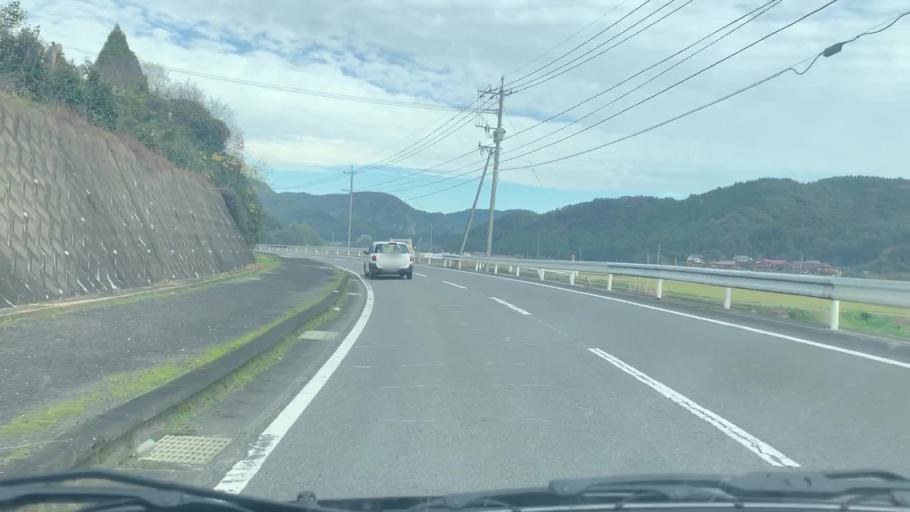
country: JP
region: Saga Prefecture
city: Imaricho-ko
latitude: 33.3124
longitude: 129.9715
